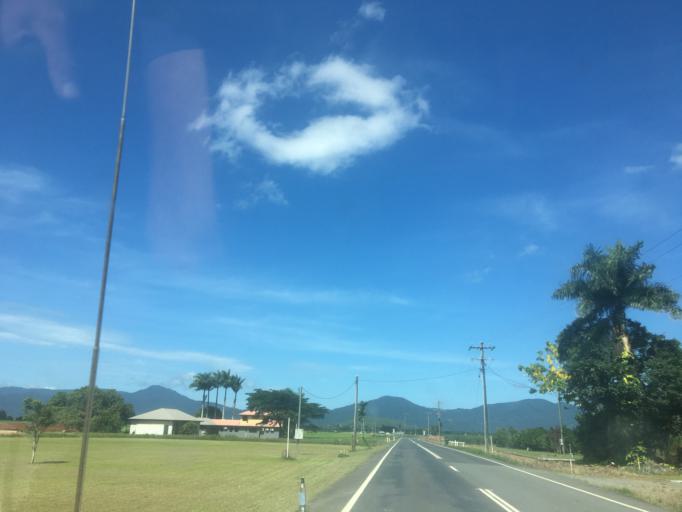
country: AU
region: Queensland
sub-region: Cairns
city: Woree
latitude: -17.0613
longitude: 145.7629
